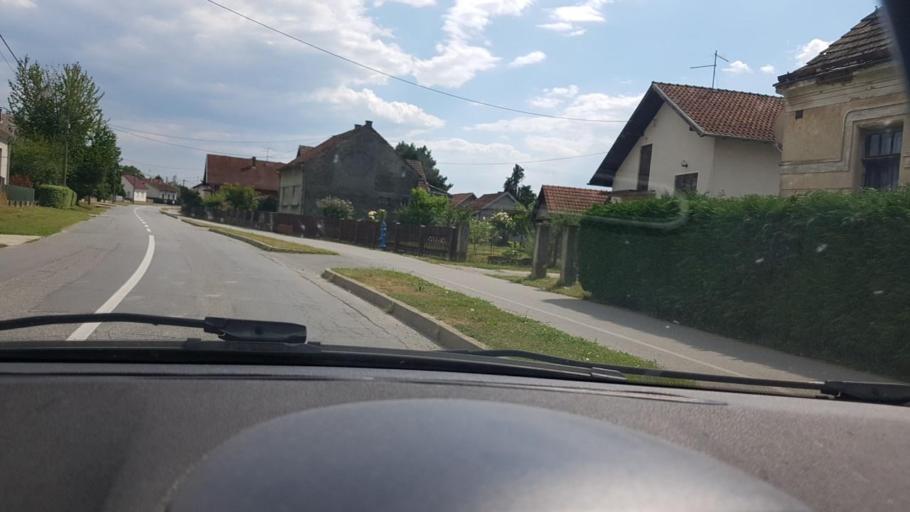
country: HR
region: Bjelovarsko-Bilogorska
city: Bjelovar
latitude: 45.9193
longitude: 16.8472
